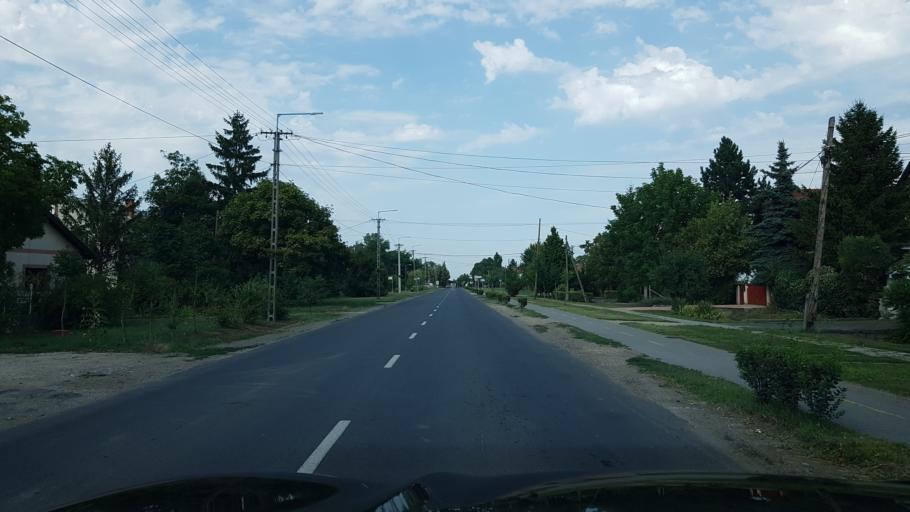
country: HU
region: Bekes
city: Fuzesgyarmat
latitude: 47.0918
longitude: 21.2034
